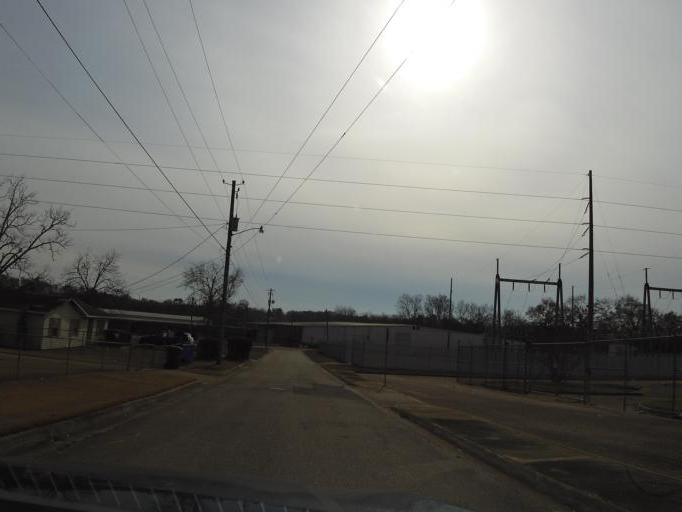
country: US
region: Alabama
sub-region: Houston County
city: Dothan
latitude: 31.2264
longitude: -85.3858
